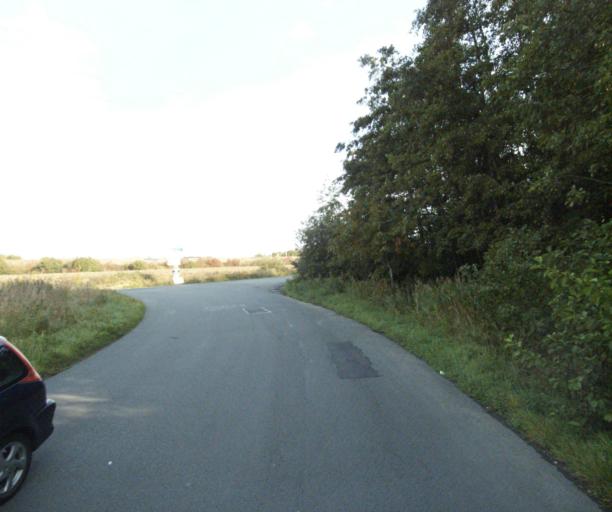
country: FR
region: Nord-Pas-de-Calais
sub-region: Departement du Nord
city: Lomme
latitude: 50.6567
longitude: 2.9788
